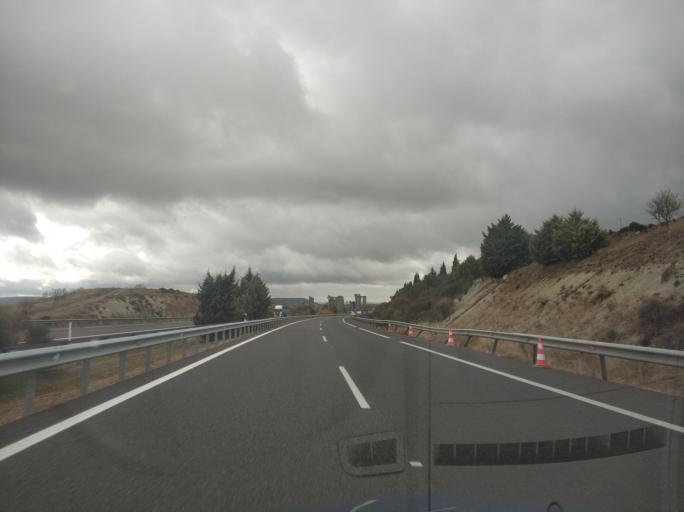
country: ES
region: Castille and Leon
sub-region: Provincia de Palencia
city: Soto de Cerrato
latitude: 41.9581
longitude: -4.4583
